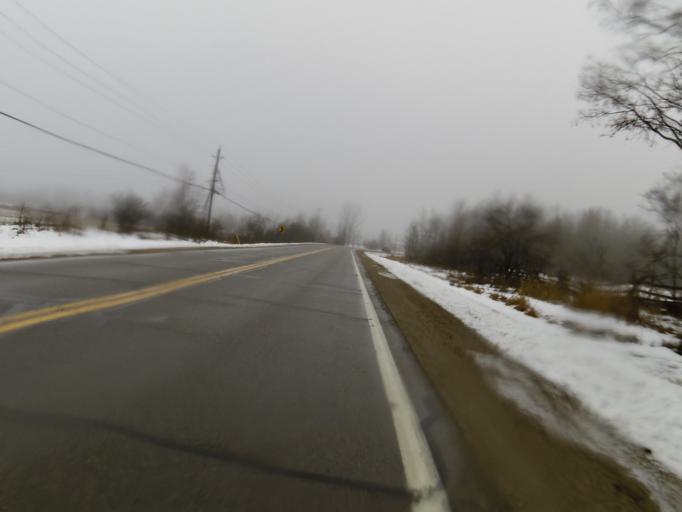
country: CA
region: Ontario
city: Perth
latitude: 44.8252
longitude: -76.3902
